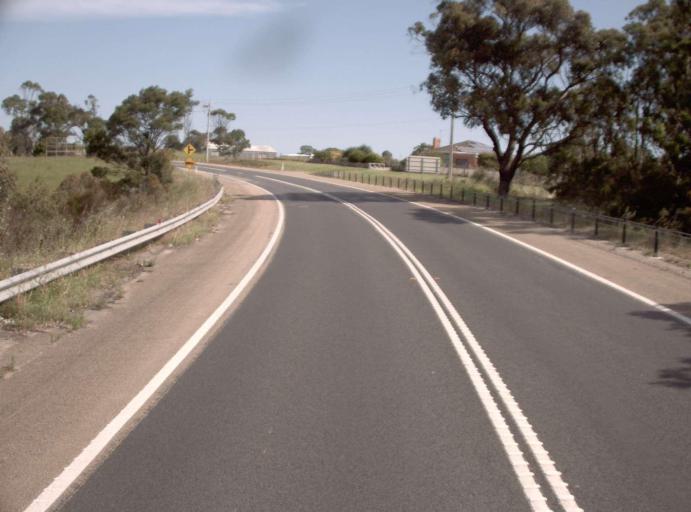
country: AU
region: Victoria
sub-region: East Gippsland
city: Lakes Entrance
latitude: -37.8635
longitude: 147.9523
